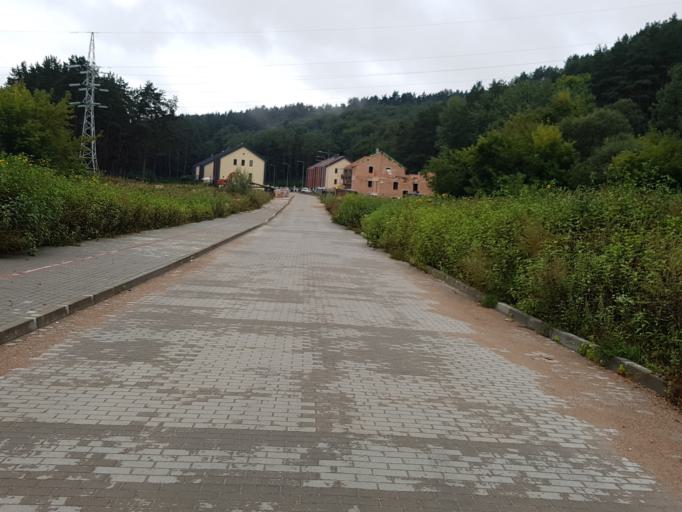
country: LT
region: Vilnius County
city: Lazdynai
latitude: 54.6665
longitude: 25.2234
